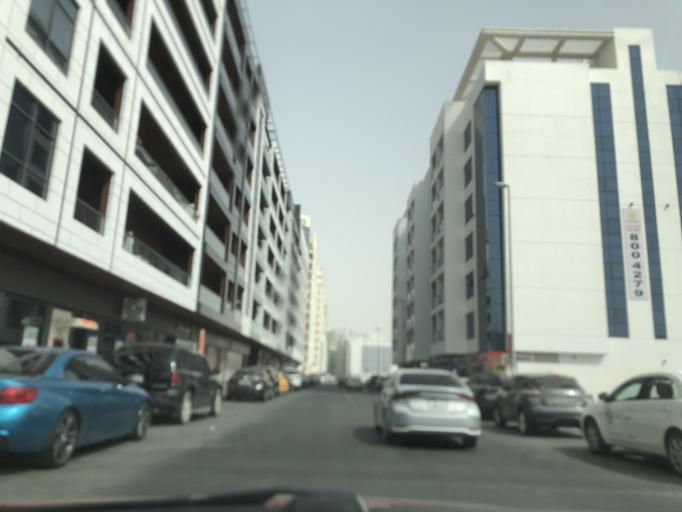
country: AE
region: Dubai
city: Dubai
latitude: 25.1116
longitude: 55.1945
